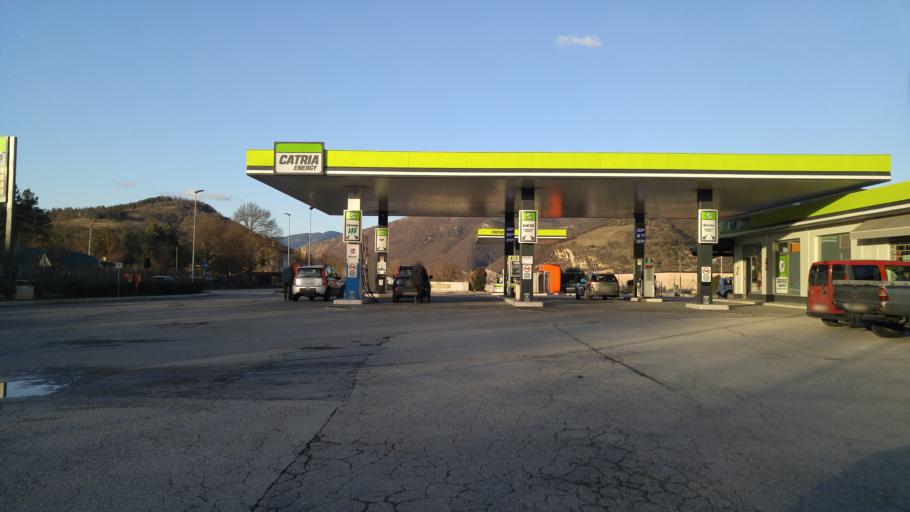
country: IT
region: The Marches
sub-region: Provincia di Pesaro e Urbino
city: Cagli
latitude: 43.5787
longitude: 12.6694
